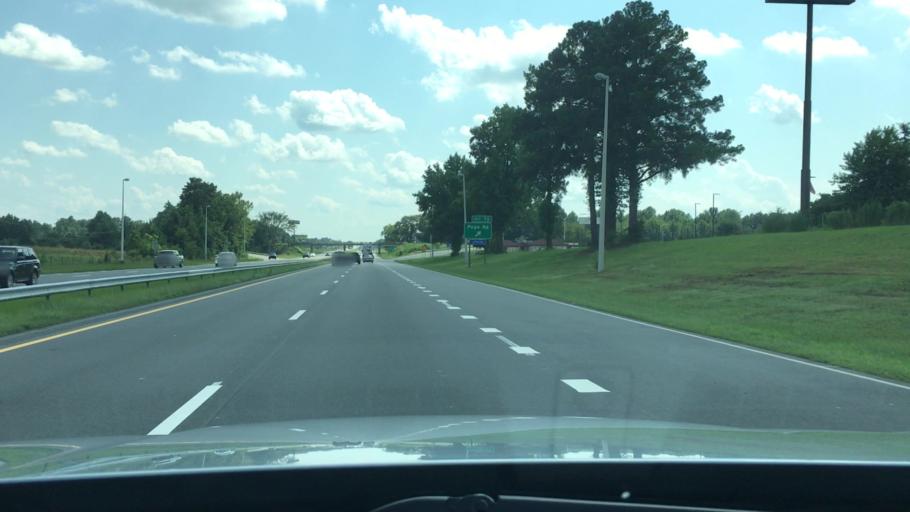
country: US
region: North Carolina
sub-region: Harnett County
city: Dunn
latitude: 35.2951
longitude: -78.6023
